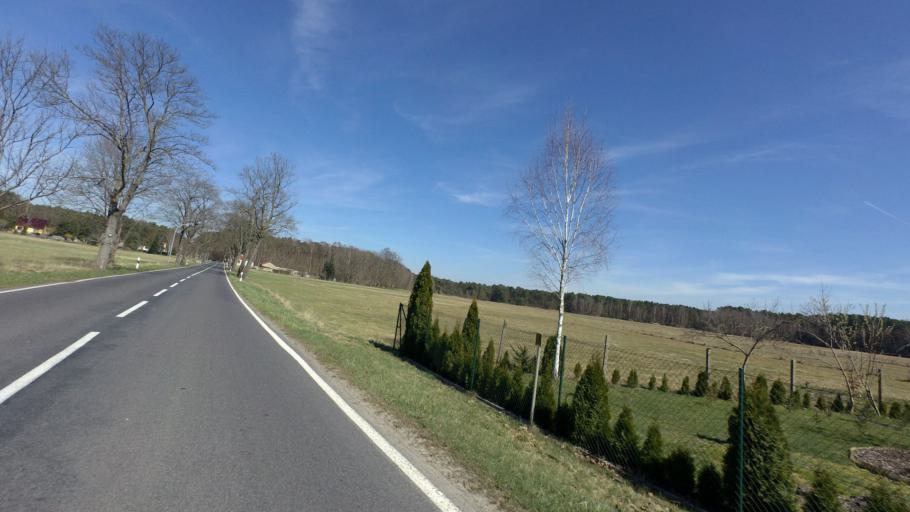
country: DE
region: Brandenburg
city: Storkow
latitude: 52.1954
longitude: 13.9205
